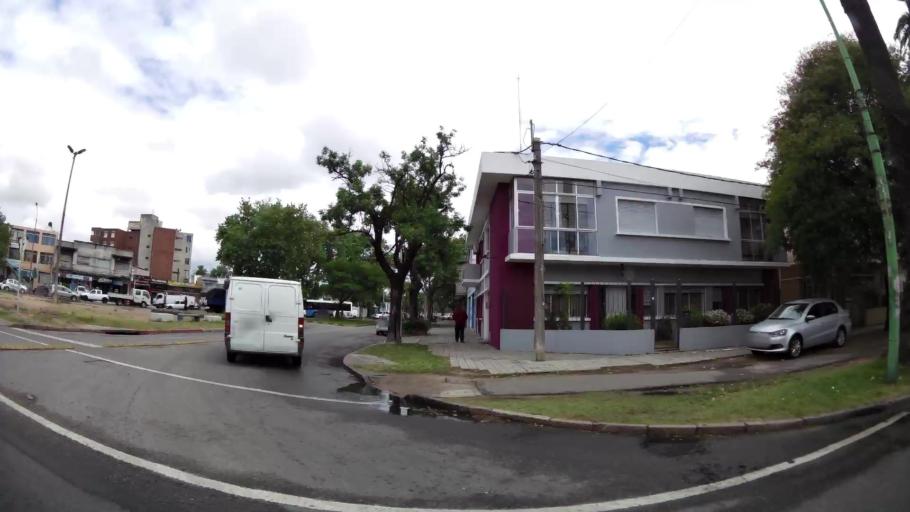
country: UY
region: Montevideo
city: Montevideo
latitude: -34.8705
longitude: -56.1754
